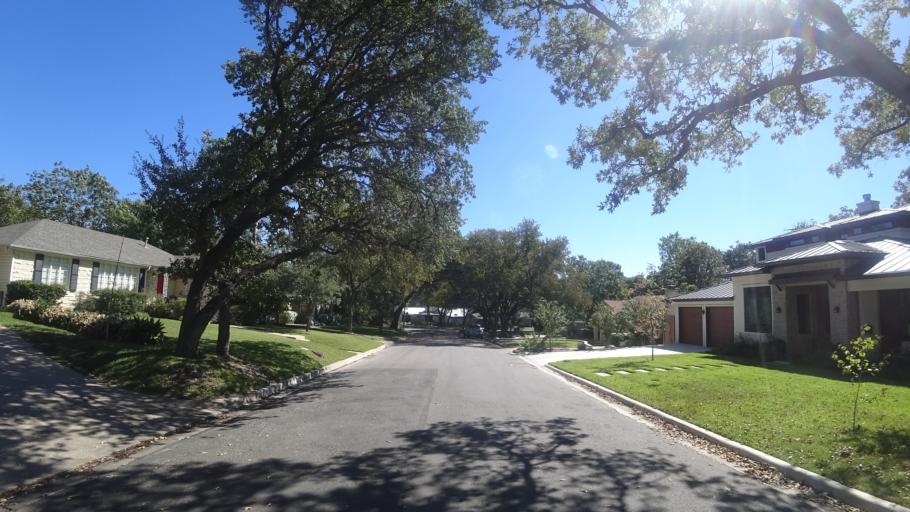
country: US
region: Texas
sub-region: Travis County
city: Austin
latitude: 30.2981
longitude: -97.7617
